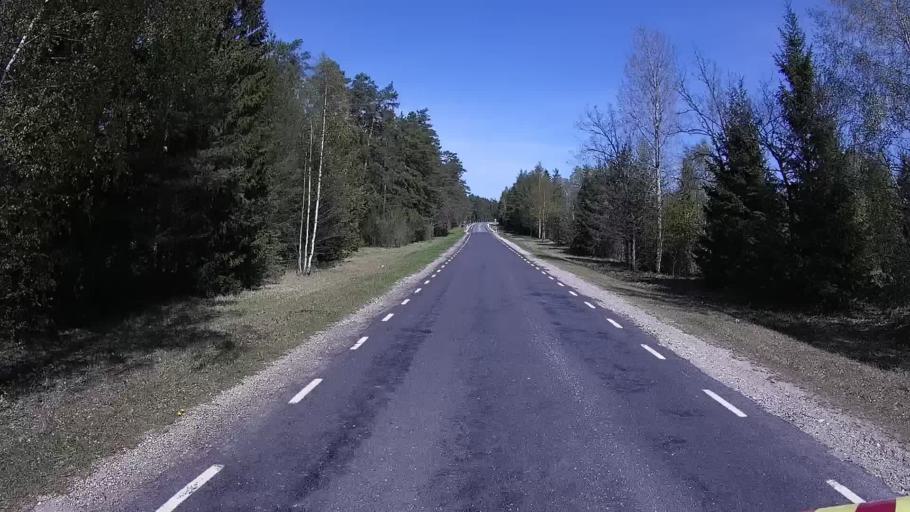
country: EE
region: Laeaene
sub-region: Ridala Parish
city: Uuemoisa
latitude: 59.0374
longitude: 23.8283
